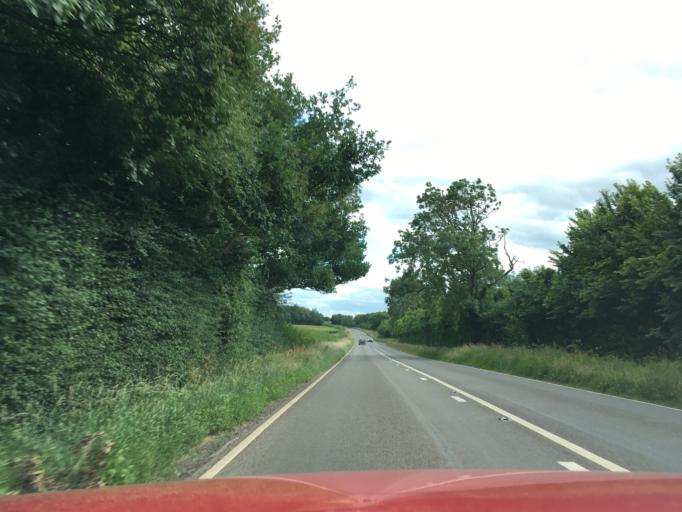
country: GB
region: England
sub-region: Leicestershire
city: Measham
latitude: 52.6645
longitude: -1.5391
